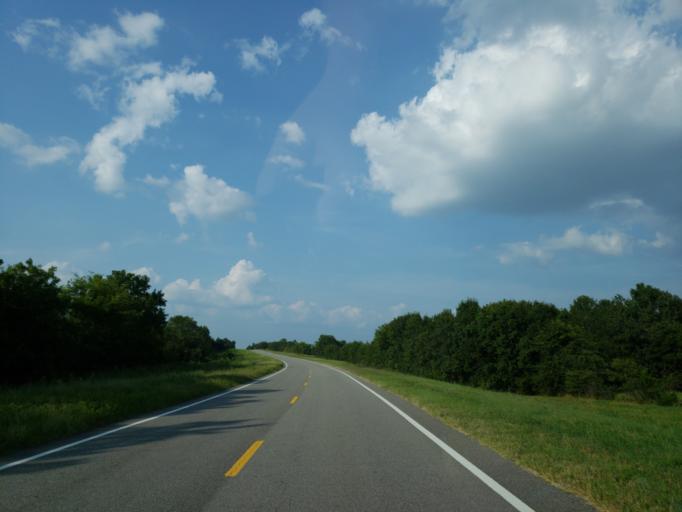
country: US
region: Alabama
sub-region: Greene County
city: Eutaw
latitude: 32.7825
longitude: -87.9782
